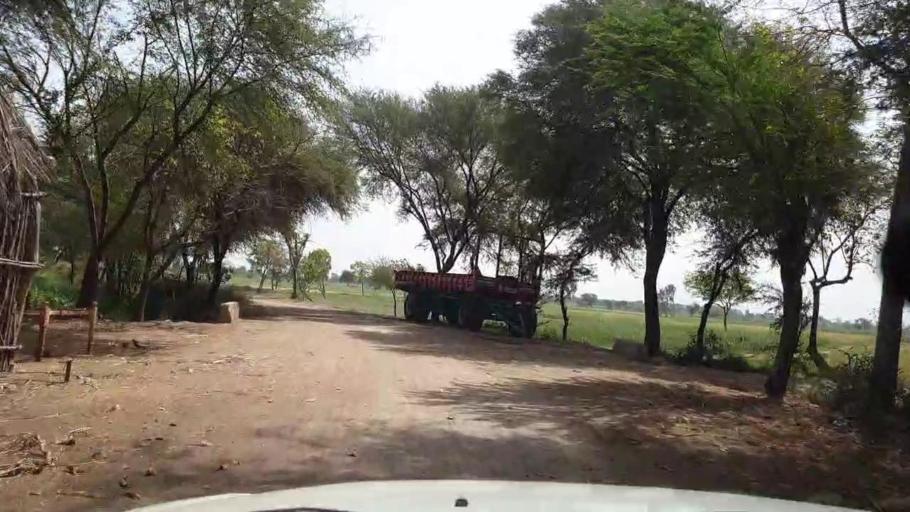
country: PK
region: Sindh
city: Matli
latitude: 25.0257
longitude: 68.7058
